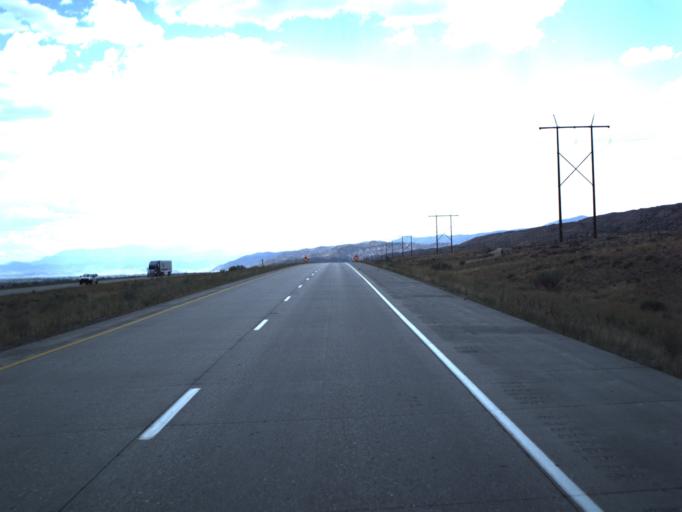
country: US
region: Utah
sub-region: Sevier County
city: Richfield
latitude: 38.8267
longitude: -112.0399
